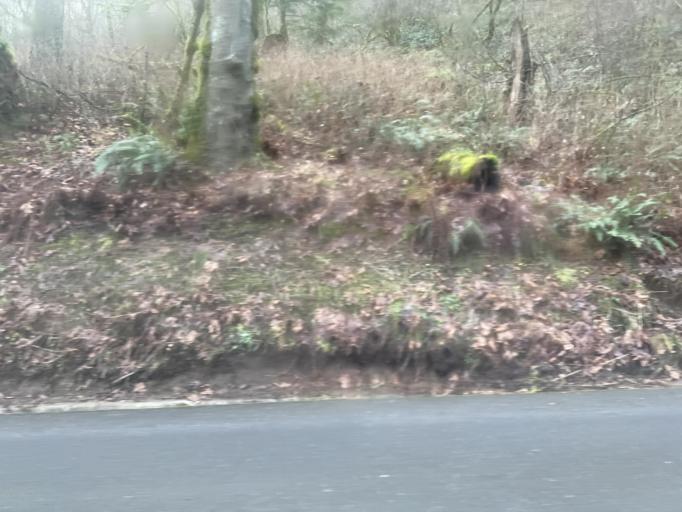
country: US
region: Washington
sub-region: Clark County
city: Washougal
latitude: 45.5340
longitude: -122.2309
